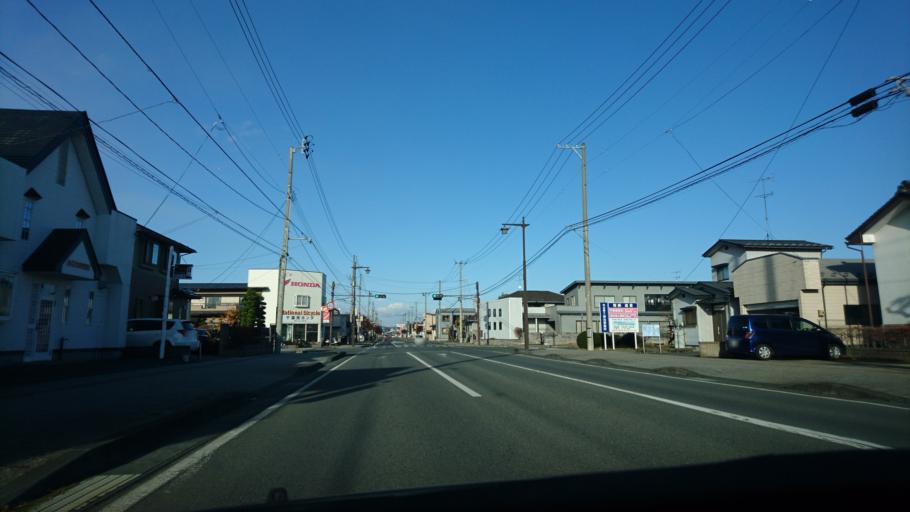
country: JP
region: Iwate
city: Mizusawa
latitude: 39.1486
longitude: 141.1410
